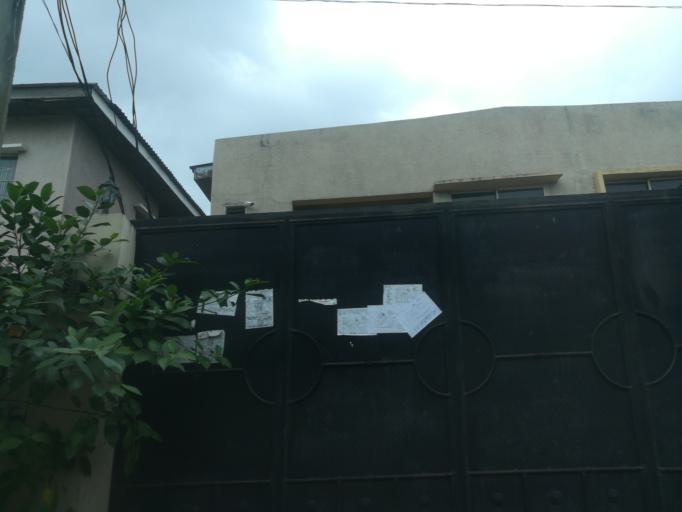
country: NG
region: Lagos
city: Ikeja
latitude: 6.5997
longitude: 3.3451
